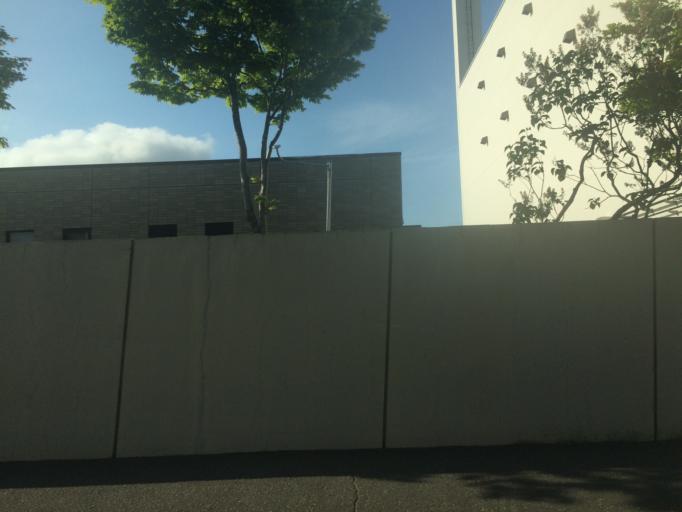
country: JP
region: Hokkaido
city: Sapporo
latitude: 43.0313
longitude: 141.3510
